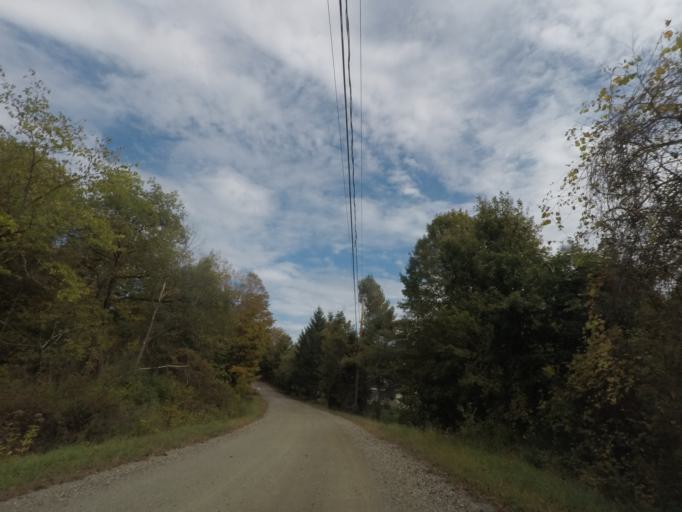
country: US
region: New York
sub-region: Rensselaer County
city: Nassau
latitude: 42.5724
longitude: -73.6227
